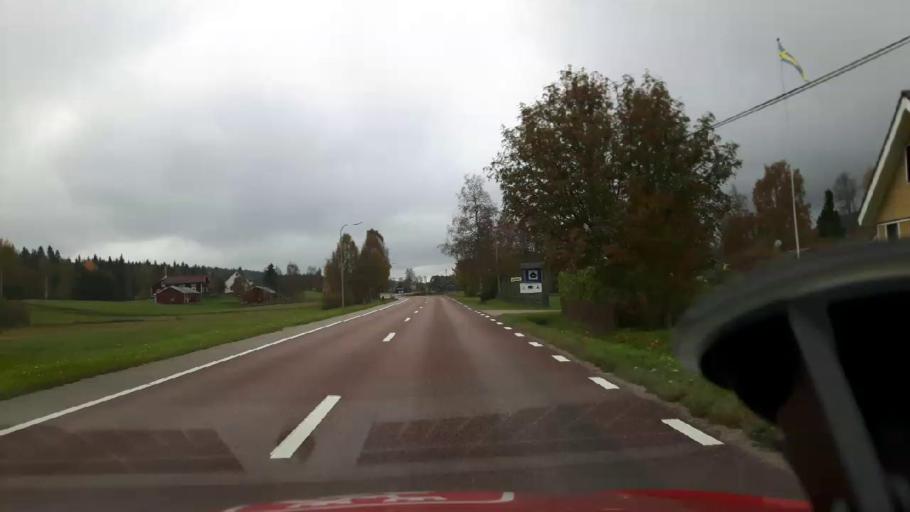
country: SE
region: Jaemtland
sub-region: Harjedalens Kommun
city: Sveg
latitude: 62.2843
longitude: 14.7992
